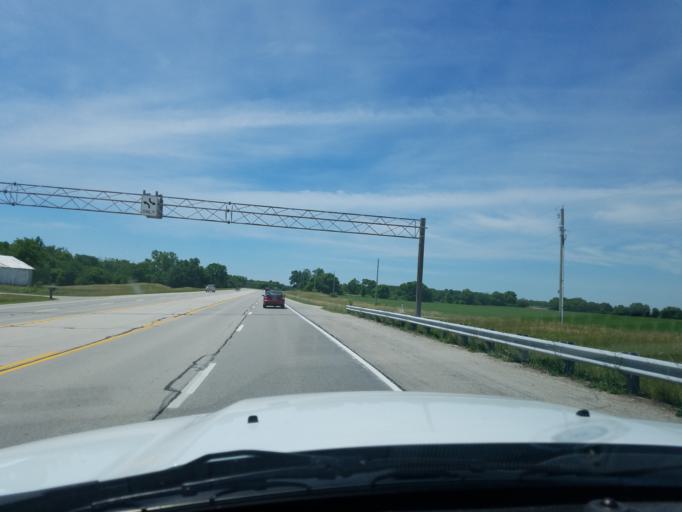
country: US
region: Indiana
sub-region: Delaware County
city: Yorktown
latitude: 40.1191
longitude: -85.4769
